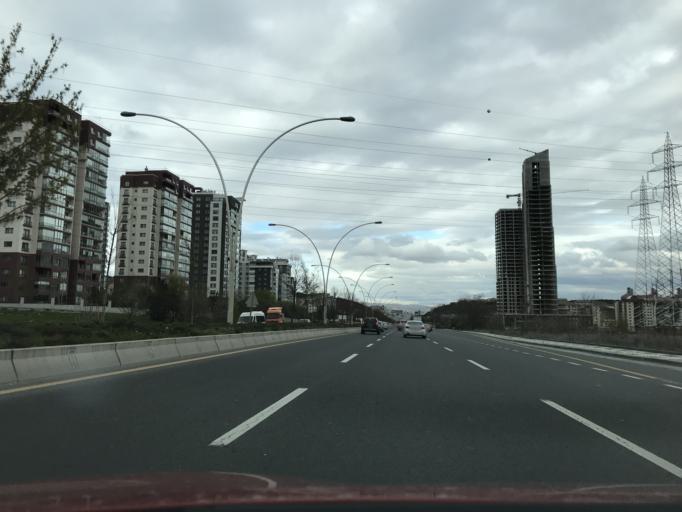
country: TR
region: Ankara
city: Etimesgut
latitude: 39.8817
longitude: 32.6592
